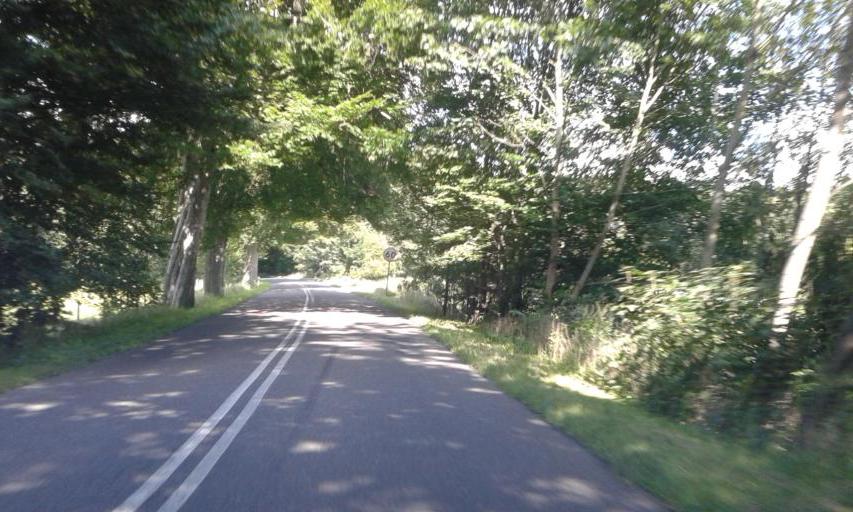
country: PL
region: West Pomeranian Voivodeship
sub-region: Powiat slawienski
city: Slawno
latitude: 54.2527
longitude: 16.6867
